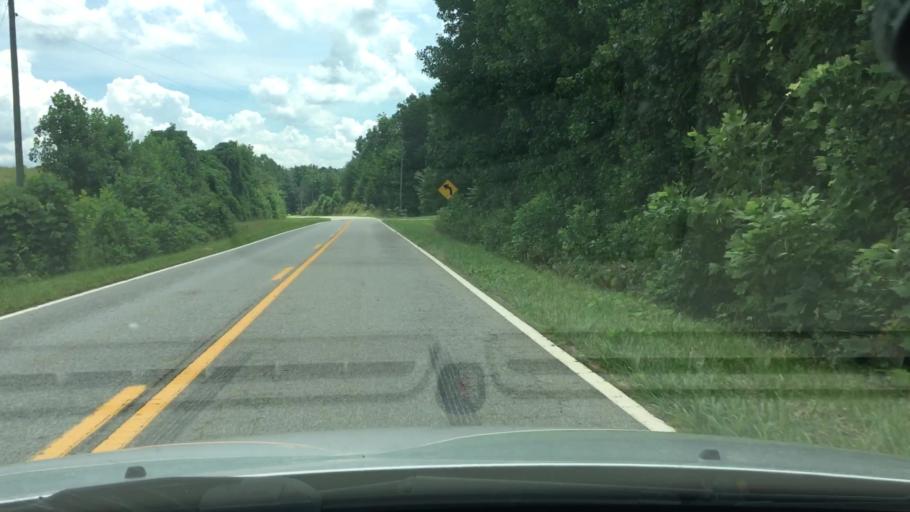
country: US
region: Georgia
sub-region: Lumpkin County
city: Dahlonega
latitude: 34.5995
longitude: -83.8959
